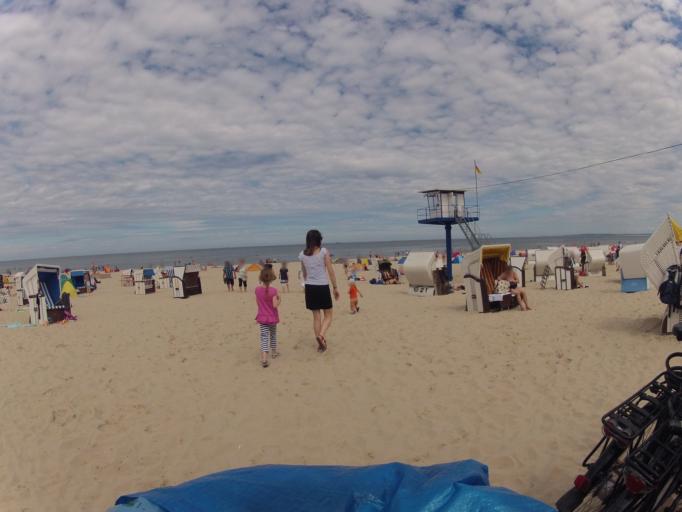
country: DE
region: Mecklenburg-Vorpommern
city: Seebad Heringsdorf
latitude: 53.9393
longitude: 14.1976
